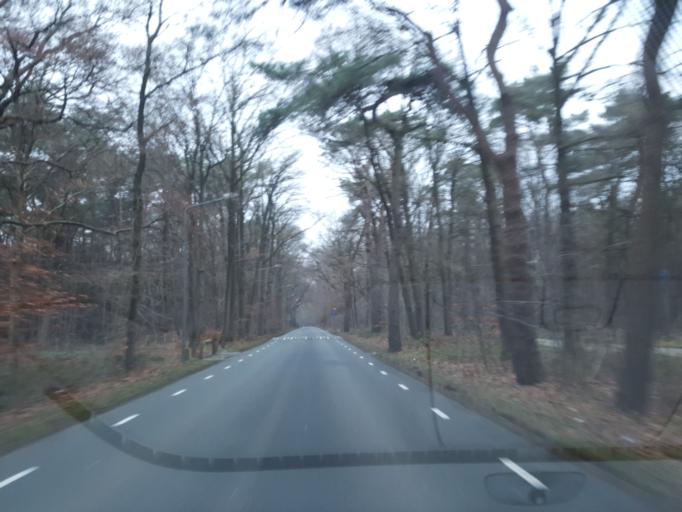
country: NL
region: North Holland
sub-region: Gemeente Wijdemeren
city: Nieuw-Loosdrecht
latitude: 52.1852
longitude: 5.1734
